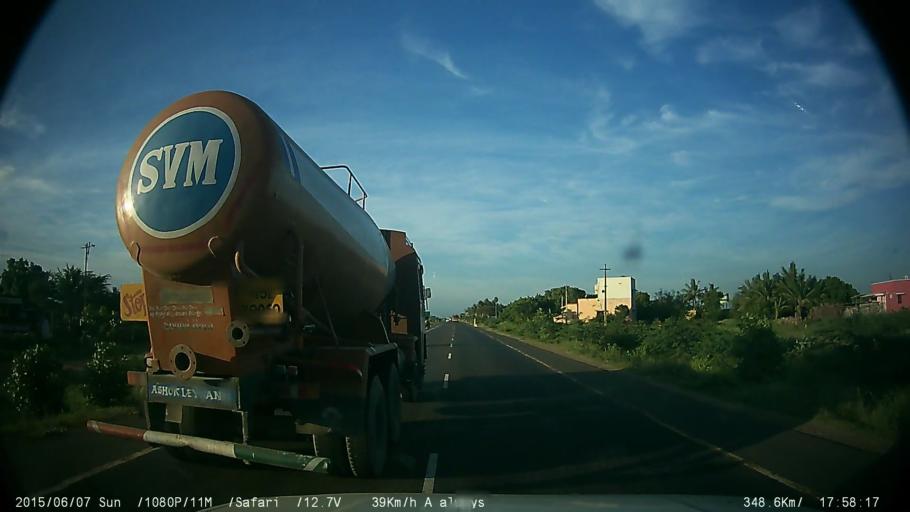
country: IN
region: Tamil Nadu
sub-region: Coimbatore
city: Singanallur
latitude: 10.9658
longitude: 77.0317
